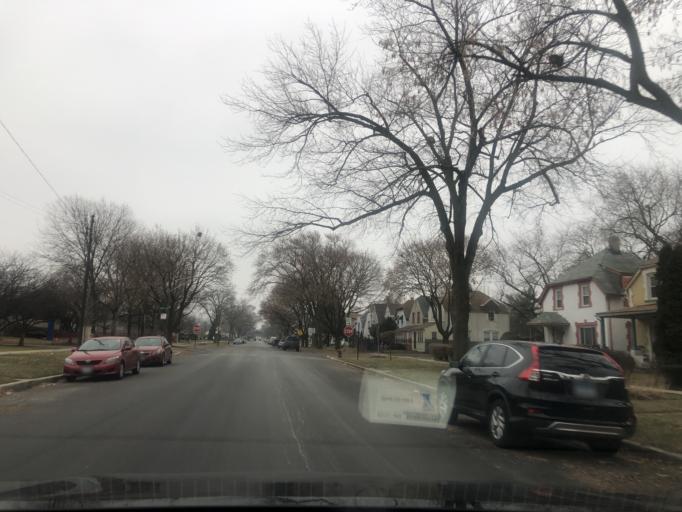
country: US
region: Illinois
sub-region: Cook County
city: Calumet Park
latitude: 41.7352
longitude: -87.6193
